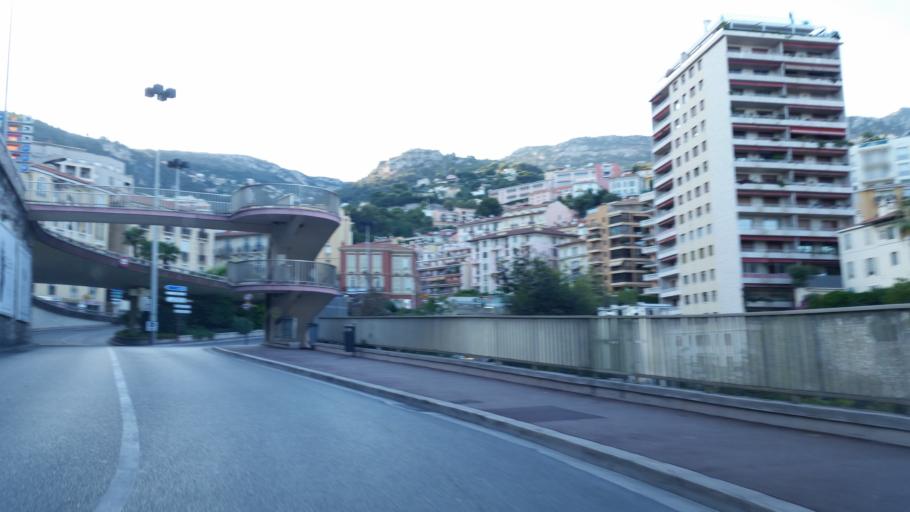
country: MC
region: Commune de Monaco
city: La Condamine
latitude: 43.7376
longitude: 7.4200
